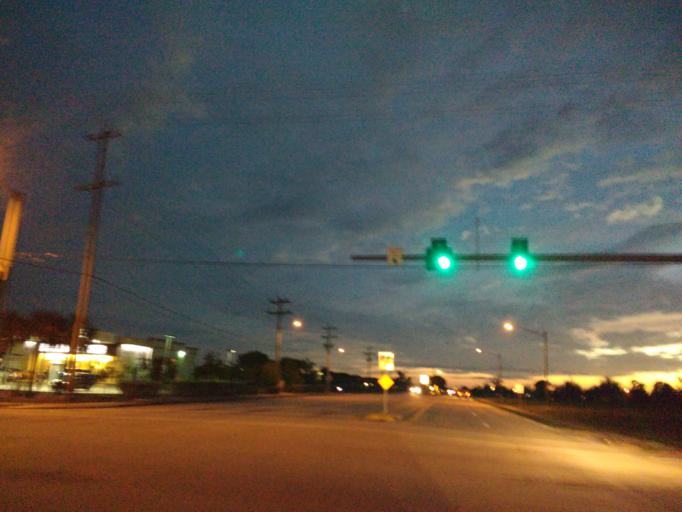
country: US
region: Florida
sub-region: Lee County
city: Cape Coral
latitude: 26.6231
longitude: -81.9914
